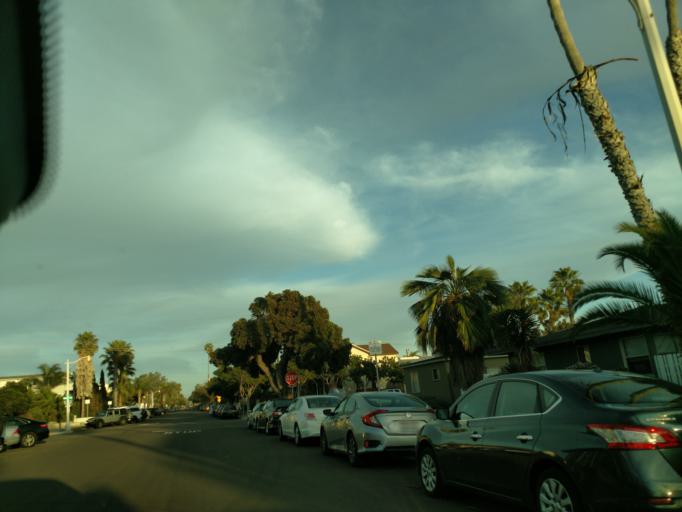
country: US
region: California
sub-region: San Diego County
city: La Jolla
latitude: 32.7997
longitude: -117.2550
